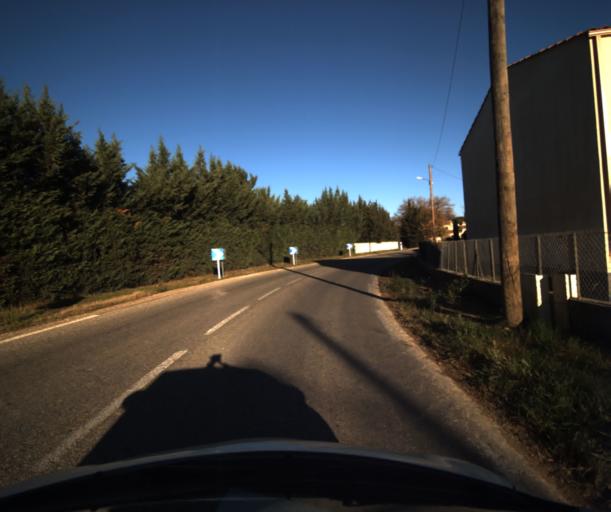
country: FR
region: Provence-Alpes-Cote d'Azur
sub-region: Departement du Vaucluse
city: Pertuis
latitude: 43.7049
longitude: 5.4951
